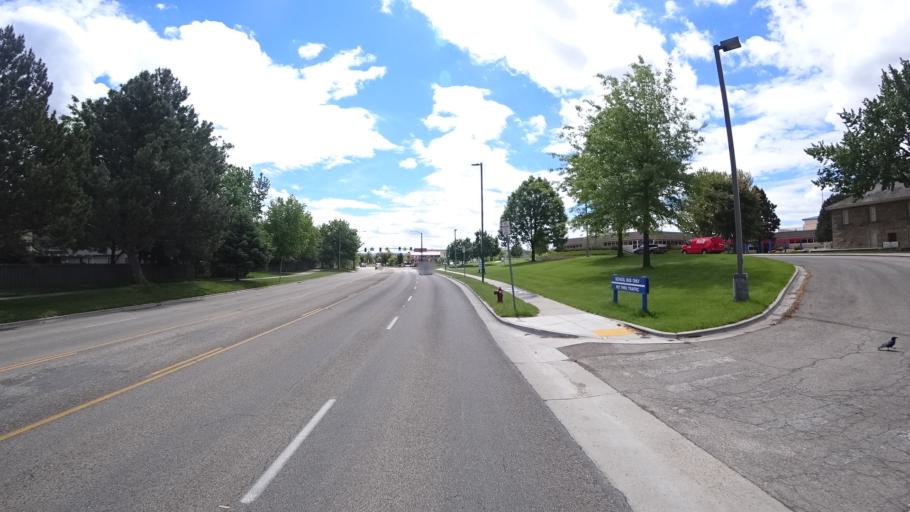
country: US
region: Idaho
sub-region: Ada County
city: Boise
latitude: 43.5765
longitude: -116.1573
